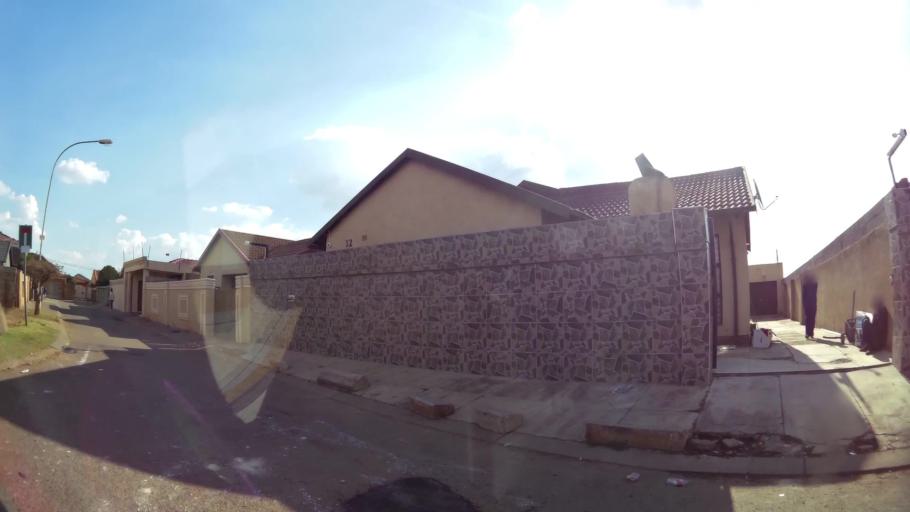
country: ZA
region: Gauteng
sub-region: City of Johannesburg Metropolitan Municipality
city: Roodepoort
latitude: -26.2133
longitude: 27.8628
